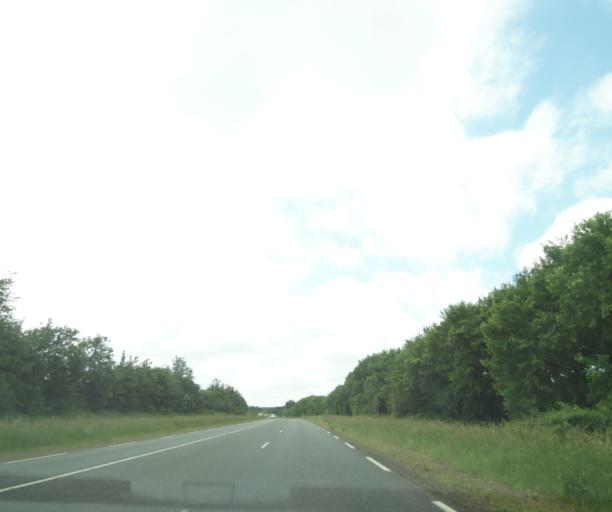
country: FR
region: Poitou-Charentes
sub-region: Departement des Deux-Sevres
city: Airvault
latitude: 46.8153
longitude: -0.2082
